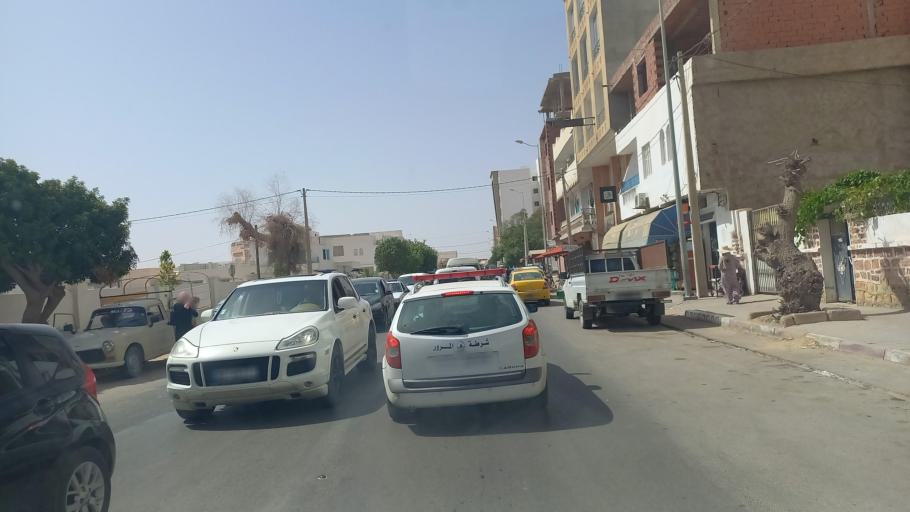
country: TN
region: Madanin
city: Medenine
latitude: 33.3403
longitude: 10.4876
